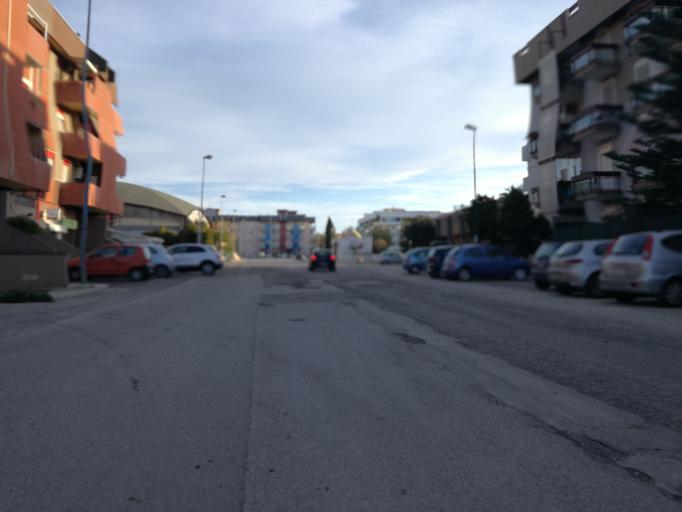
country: IT
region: Apulia
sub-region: Provincia di Bari
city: Valenzano
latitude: 41.0472
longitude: 16.8879
